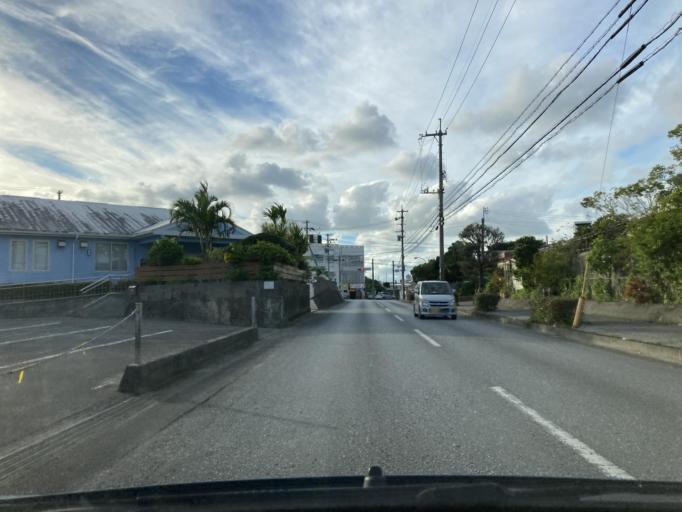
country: JP
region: Okinawa
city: Tomigusuku
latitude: 26.1475
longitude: 127.7259
